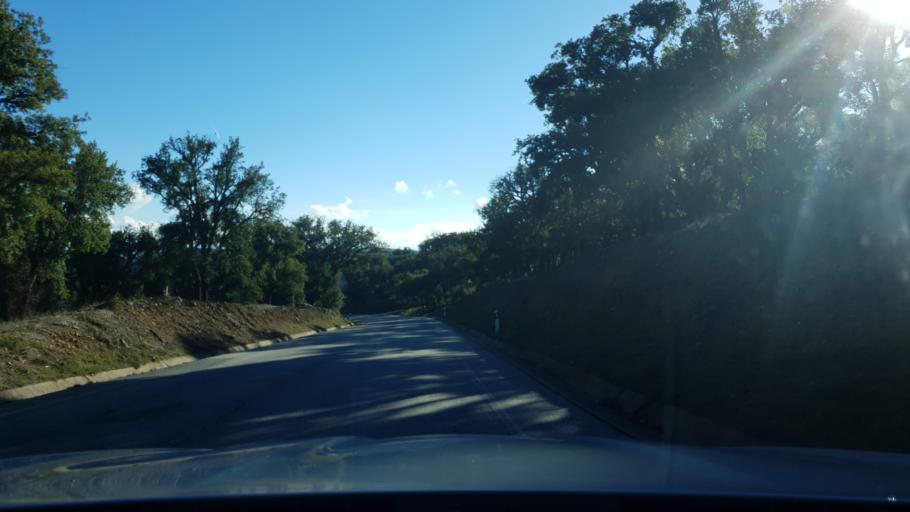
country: PT
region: Braganca
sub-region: Freixo de Espada A Cinta
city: Freixo de Espada a Cinta
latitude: 41.0985
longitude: -6.8319
